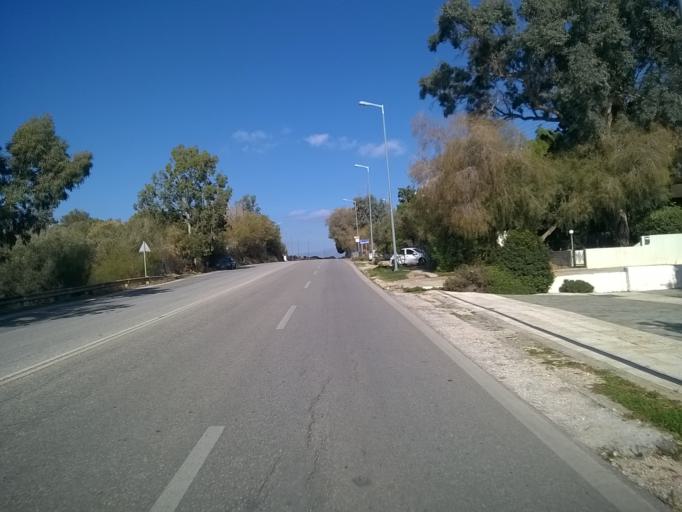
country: GR
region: Attica
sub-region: Nomarchia Anatolikis Attikis
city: Saronida
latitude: 37.7438
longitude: 23.9042
